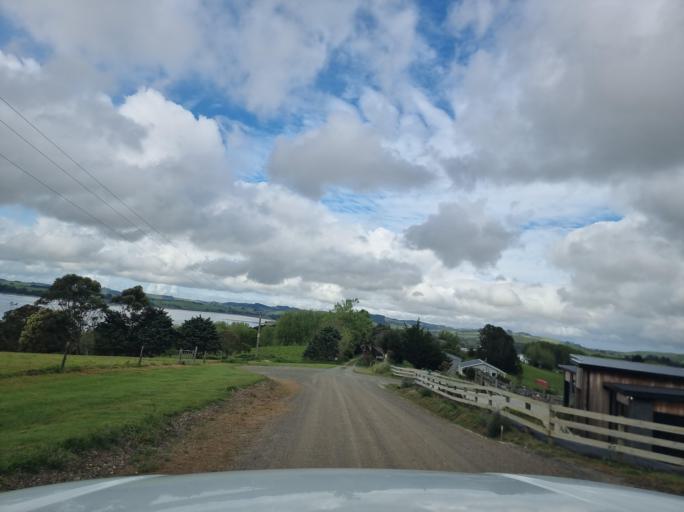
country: NZ
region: Northland
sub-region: Whangarei
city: Ruakaka
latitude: -36.1316
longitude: 174.2080
